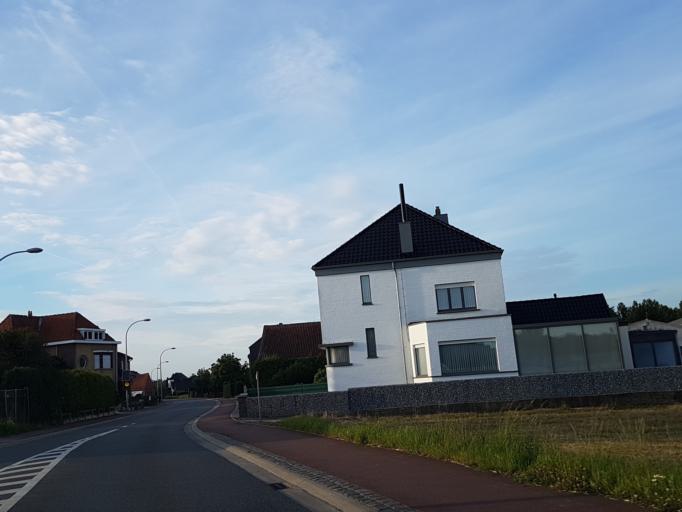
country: BE
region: Flanders
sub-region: Provincie Vlaams-Brabant
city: Merchtem
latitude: 50.9868
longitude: 4.2588
